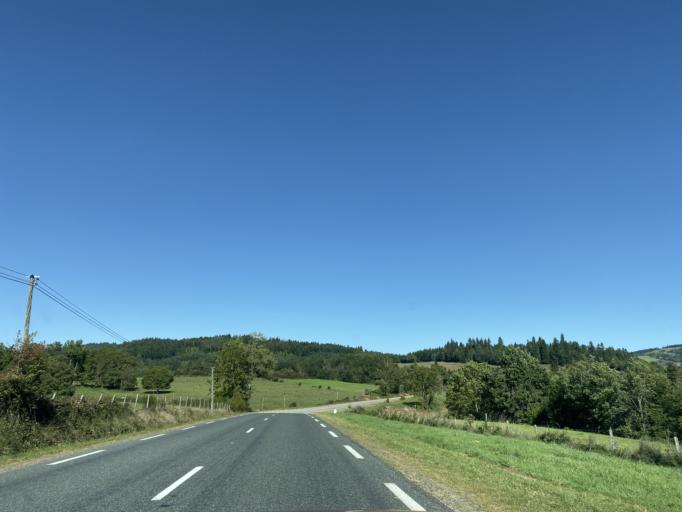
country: FR
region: Rhone-Alpes
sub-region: Departement de la Loire
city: Saint-Just-en-Chevalet
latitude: 45.8885
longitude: 3.8438
